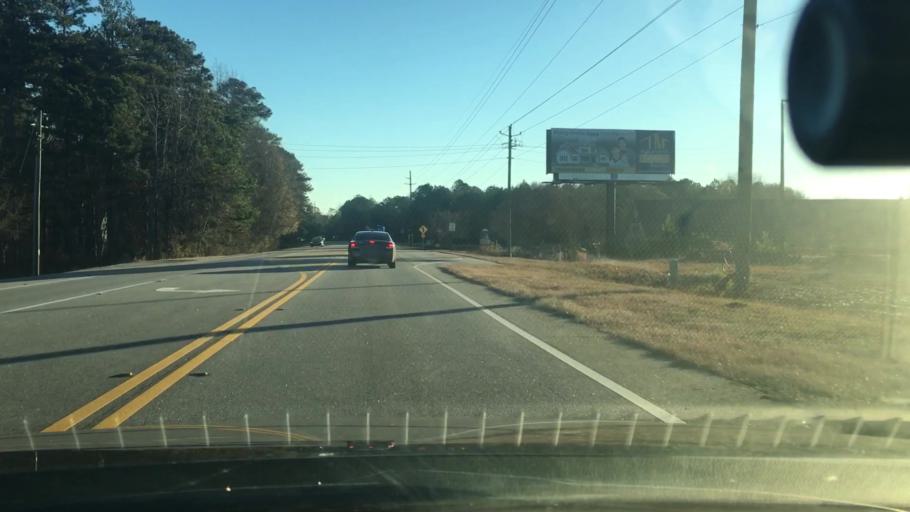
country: US
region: Georgia
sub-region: Coweta County
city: Senoia
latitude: 33.2935
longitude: -84.5727
